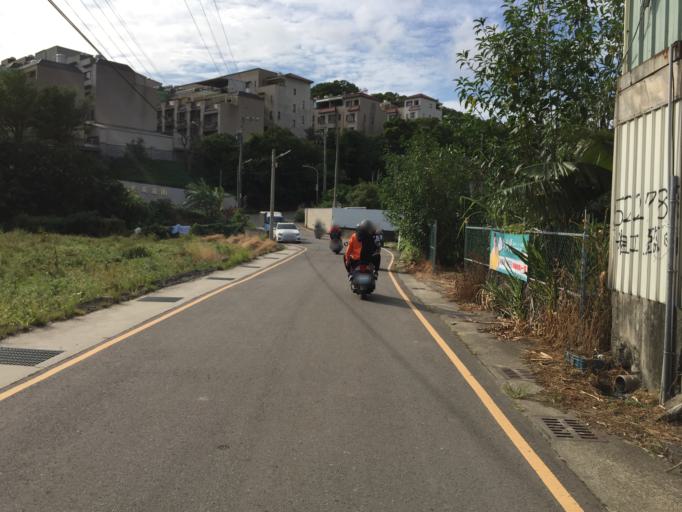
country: TW
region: Taiwan
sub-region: Hsinchu
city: Hsinchu
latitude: 24.7755
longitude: 120.9315
